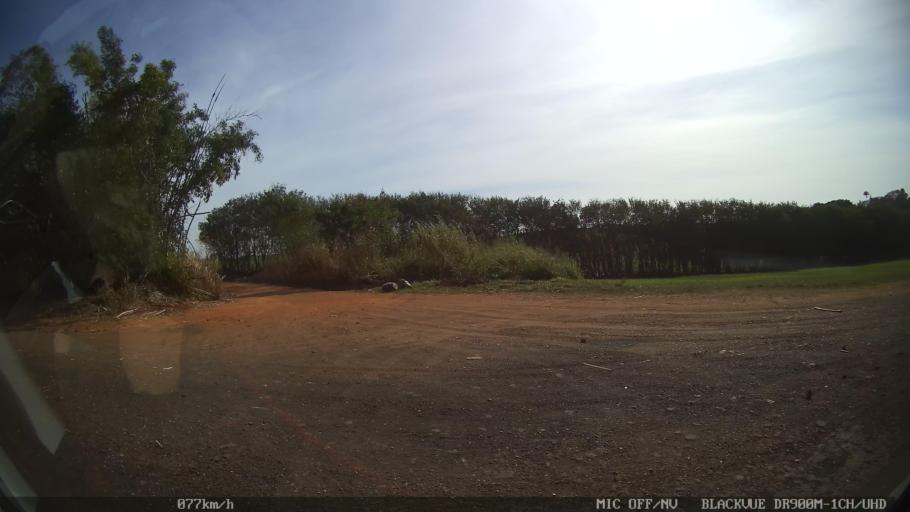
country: BR
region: Sao Paulo
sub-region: Rio Das Pedras
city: Rio das Pedras
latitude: -22.7956
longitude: -47.5945
